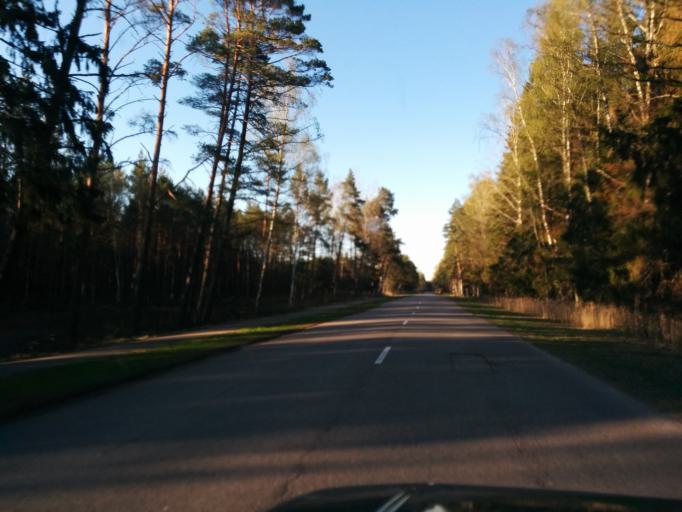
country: LV
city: Tireli
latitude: 56.9629
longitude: 23.5261
